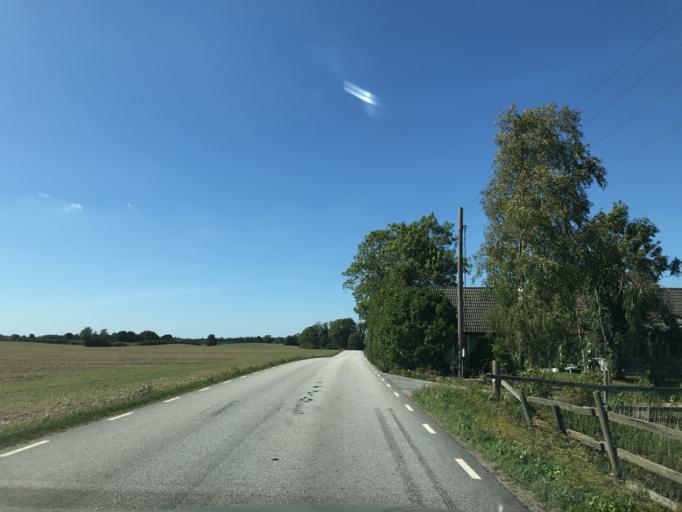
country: SE
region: Skane
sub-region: Tomelilla Kommun
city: Tomelilla
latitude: 55.6462
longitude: 13.9741
